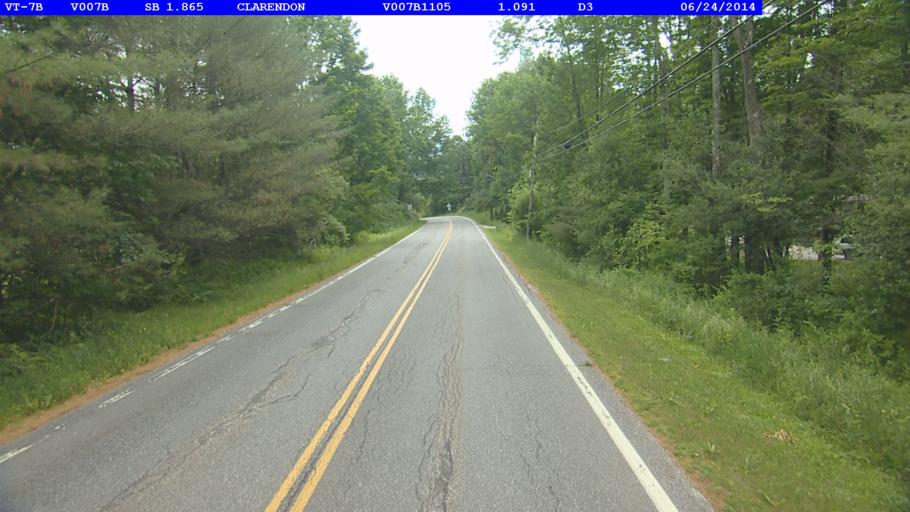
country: US
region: Vermont
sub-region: Rutland County
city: Rutland
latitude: 43.5179
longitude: -72.9659
